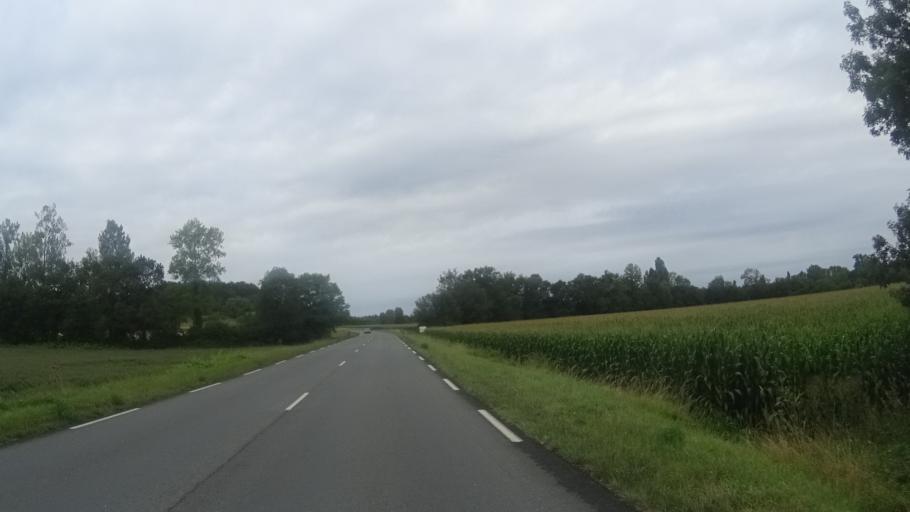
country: FR
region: Aquitaine
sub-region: Departement de la Dordogne
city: Riberac
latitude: 45.2537
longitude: 0.3836
